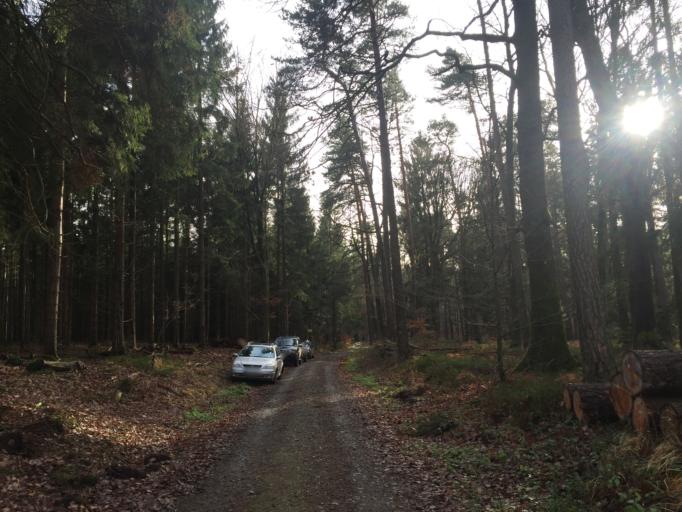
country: DE
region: Hesse
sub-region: Regierungsbezirk Darmstadt
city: Frankisch-Crumbach
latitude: 49.7043
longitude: 8.9194
